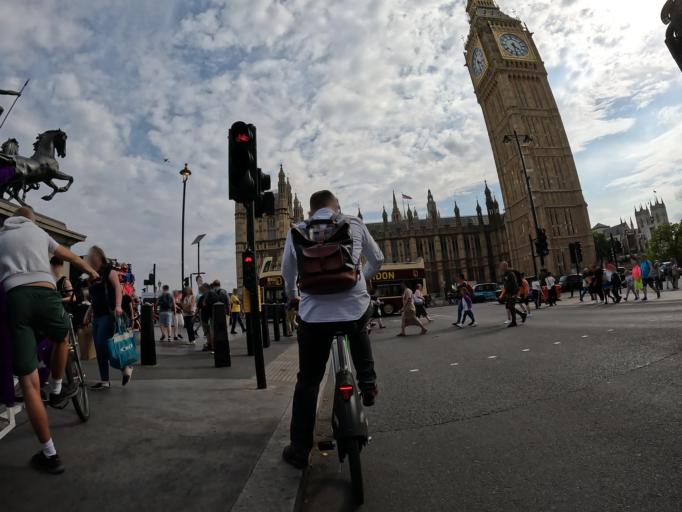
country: GB
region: England
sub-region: Kent
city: Halstead
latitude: 51.3493
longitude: 0.1136
